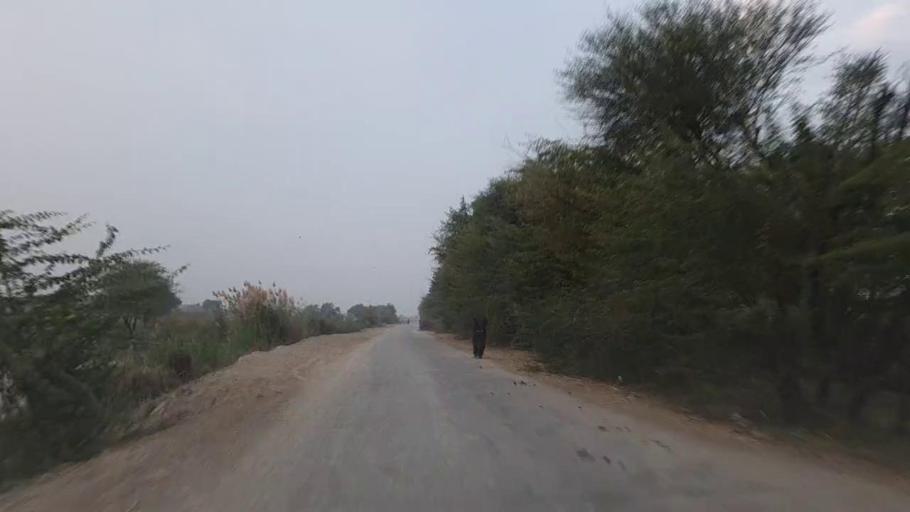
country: PK
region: Sindh
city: Jam Sahib
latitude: 26.3210
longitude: 68.5530
